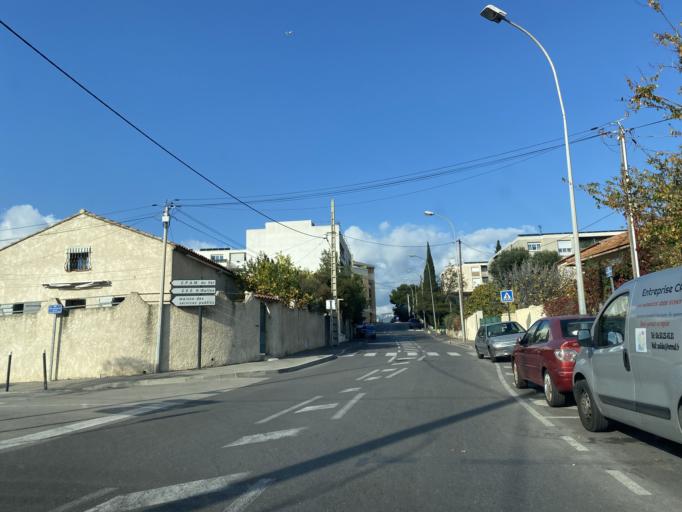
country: FR
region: Provence-Alpes-Cote d'Azur
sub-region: Departement du Var
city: La Seyne-sur-Mer
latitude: 43.1113
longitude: 5.8731
